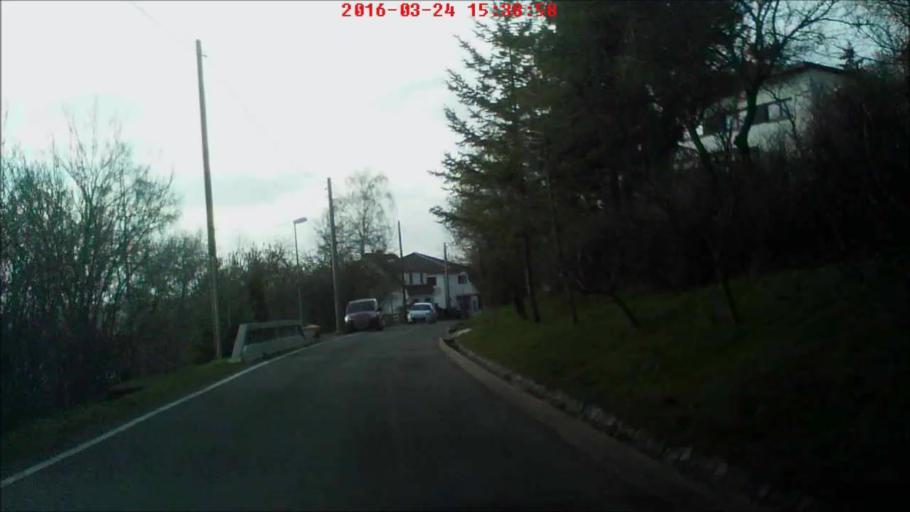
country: DE
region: Thuringia
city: Kirchheim
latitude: 50.9191
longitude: 10.9976
